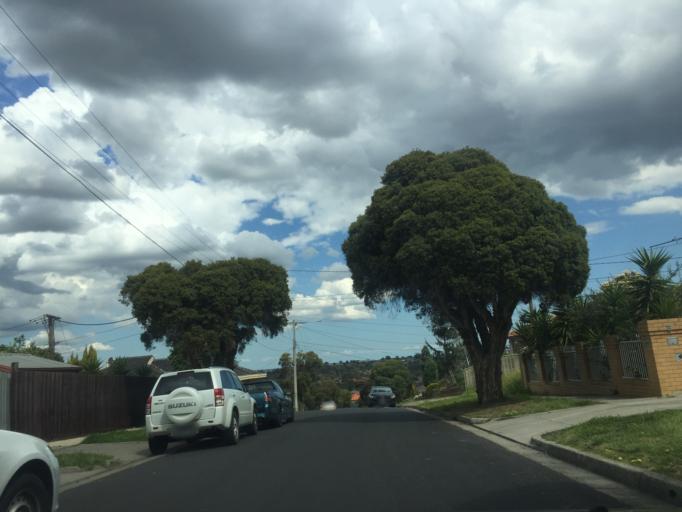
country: AU
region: Victoria
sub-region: Darebin
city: Kingsbury
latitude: -37.7077
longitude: 145.0290
